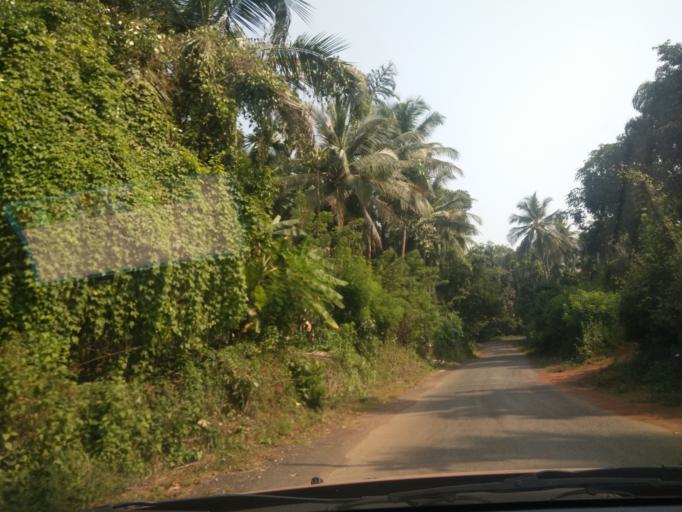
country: IN
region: Goa
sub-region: North Goa
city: Valpoy
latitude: 15.4838
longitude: 74.1385
